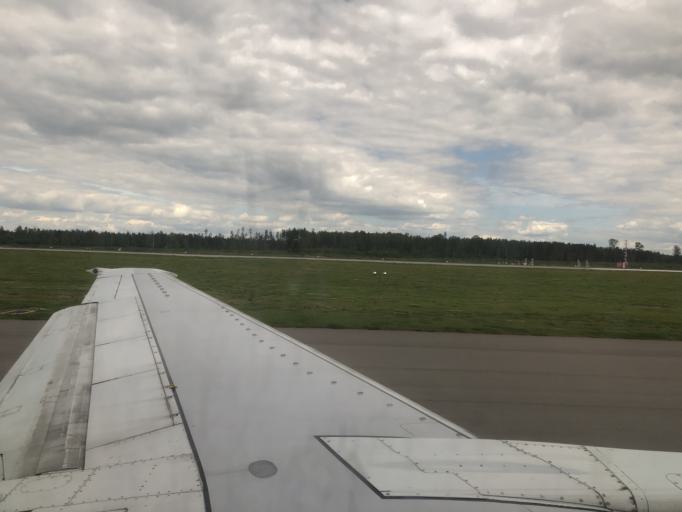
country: BY
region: Minsk
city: Smilavichy
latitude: 53.8827
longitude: 28.0632
